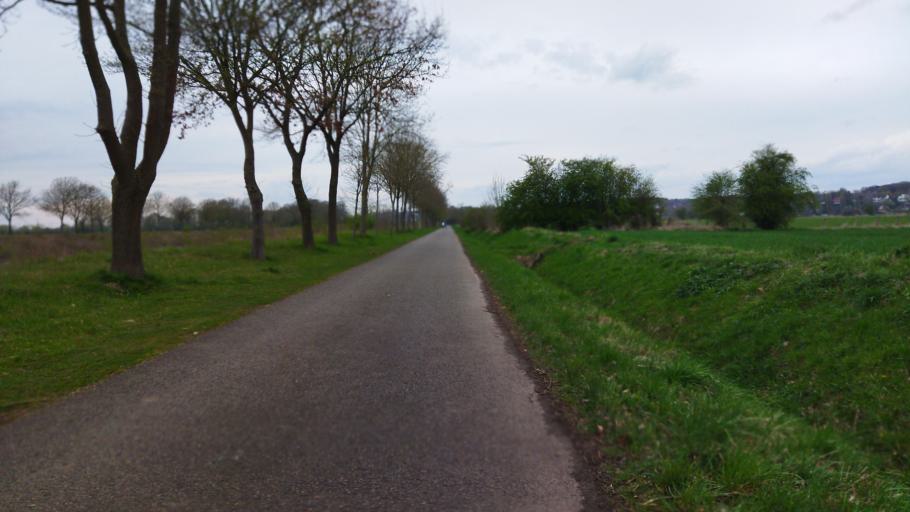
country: DE
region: Lower Saxony
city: Ahsen-Oetzen
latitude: 52.9909
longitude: 9.0976
